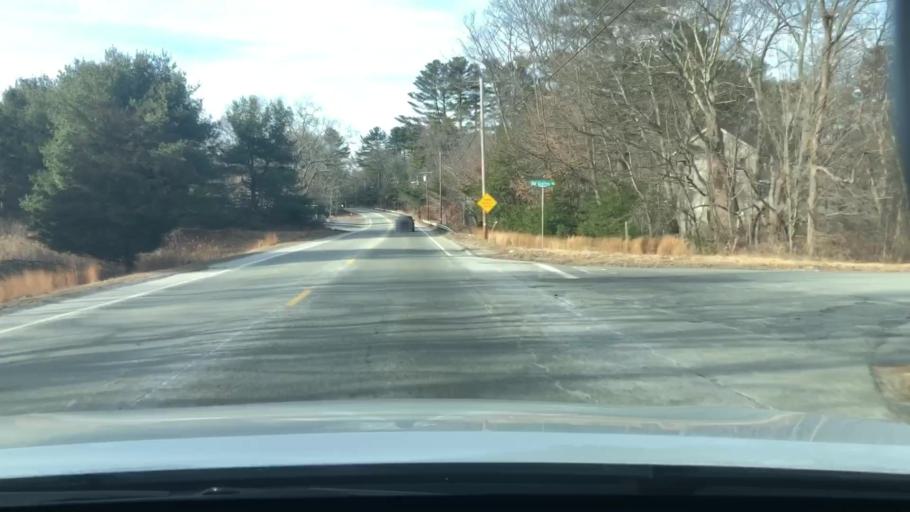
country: US
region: Massachusetts
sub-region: Worcester County
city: Northbridge
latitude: 42.1747
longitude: -71.6322
